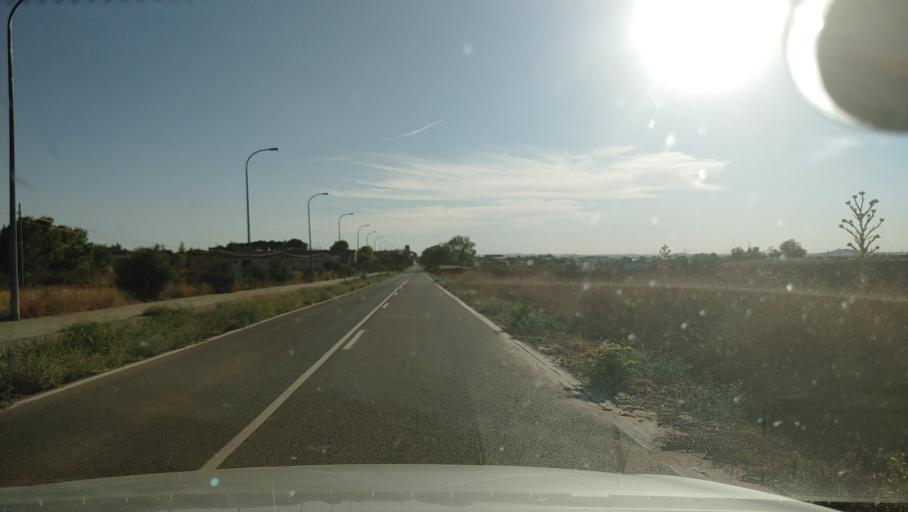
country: ES
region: Castille-La Mancha
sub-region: Provincia de Ciudad Real
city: Infantes
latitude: 38.7435
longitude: -2.9990
